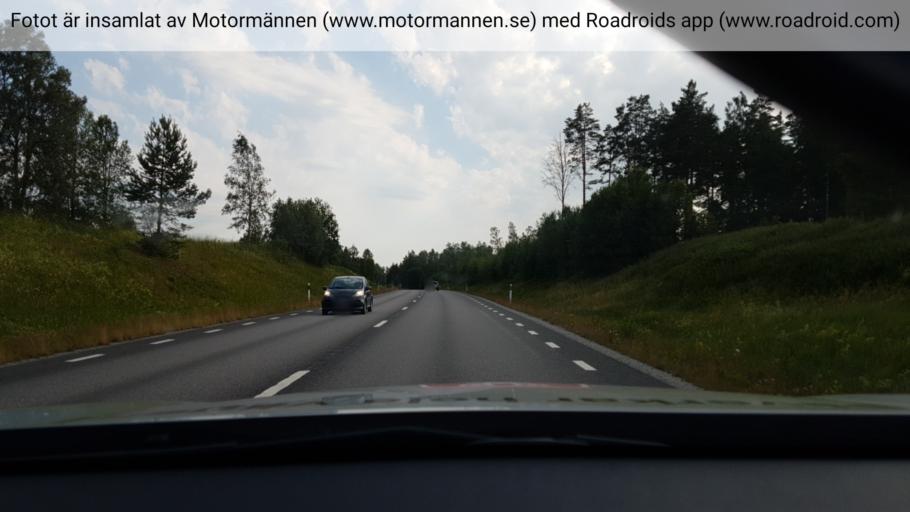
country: SE
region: Vaestra Goetaland
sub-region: Ulricehamns Kommun
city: Ulricehamn
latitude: 57.9514
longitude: 13.5170
